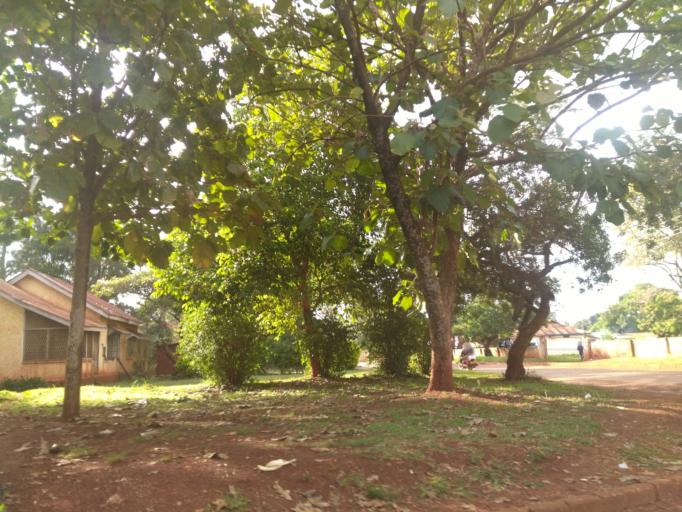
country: UG
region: Eastern Region
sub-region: Jinja District
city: Jinja
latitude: 0.4262
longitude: 33.2061
